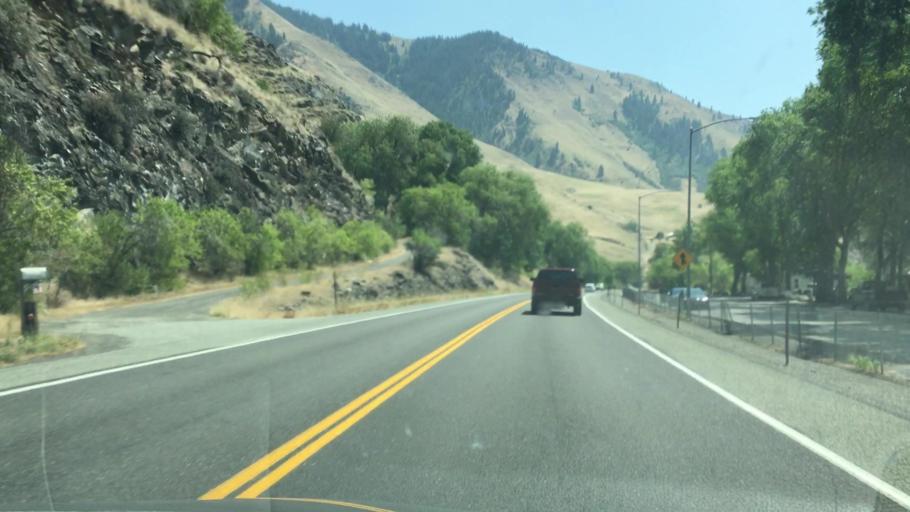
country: US
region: Idaho
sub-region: Valley County
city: McCall
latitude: 45.3434
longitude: -116.3505
